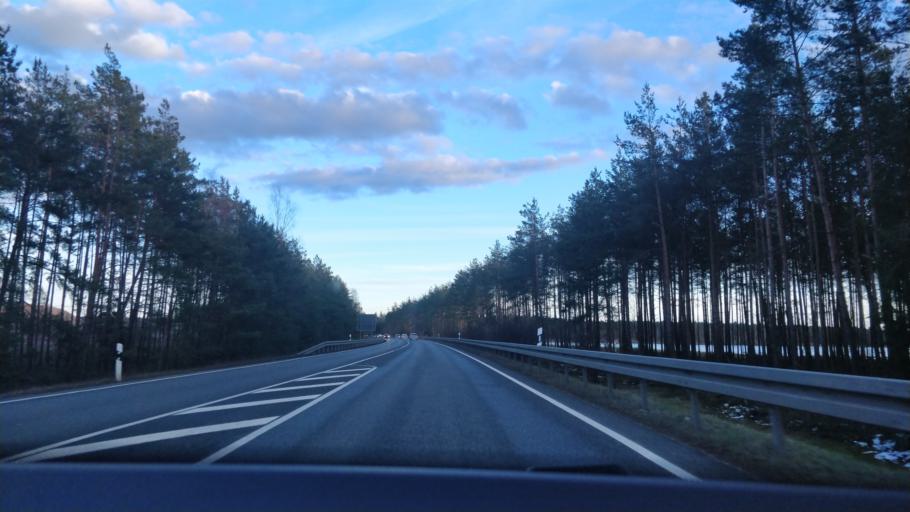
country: DE
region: Bavaria
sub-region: Upper Palatinate
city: Schwarzenbach
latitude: 49.7244
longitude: 11.9690
